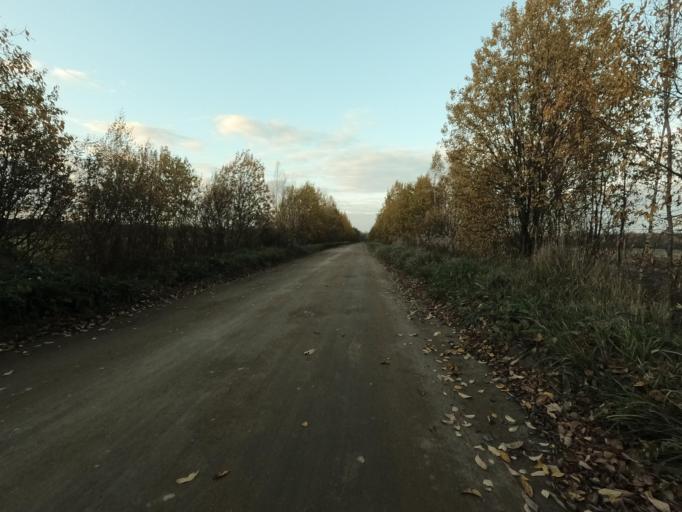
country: RU
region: Leningrad
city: Mga
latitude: 59.8019
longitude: 31.2005
